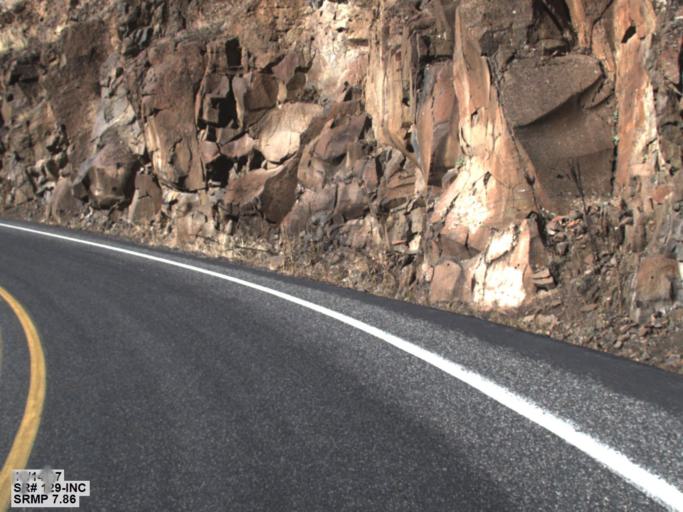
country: US
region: Washington
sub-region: Asotin County
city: Asotin
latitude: 46.0543
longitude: -117.2304
